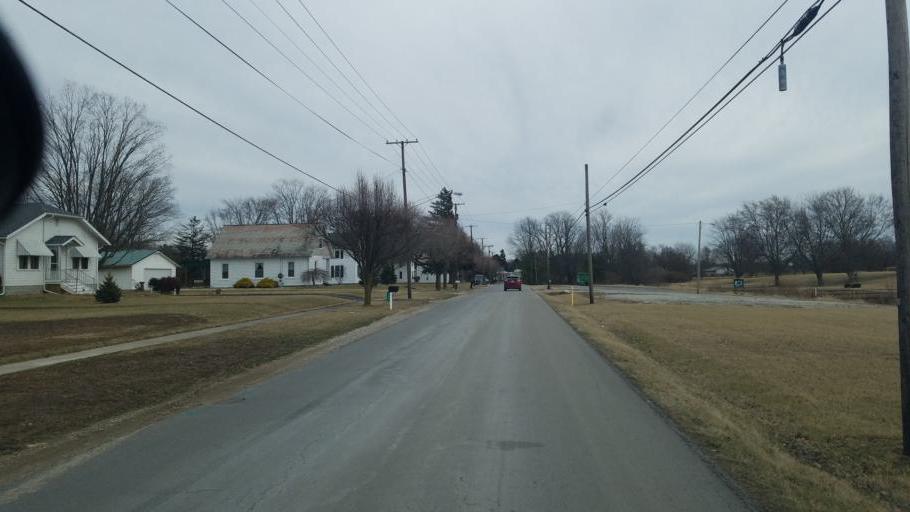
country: US
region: Ohio
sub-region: Marion County
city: Prospect
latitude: 40.4579
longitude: -83.0869
